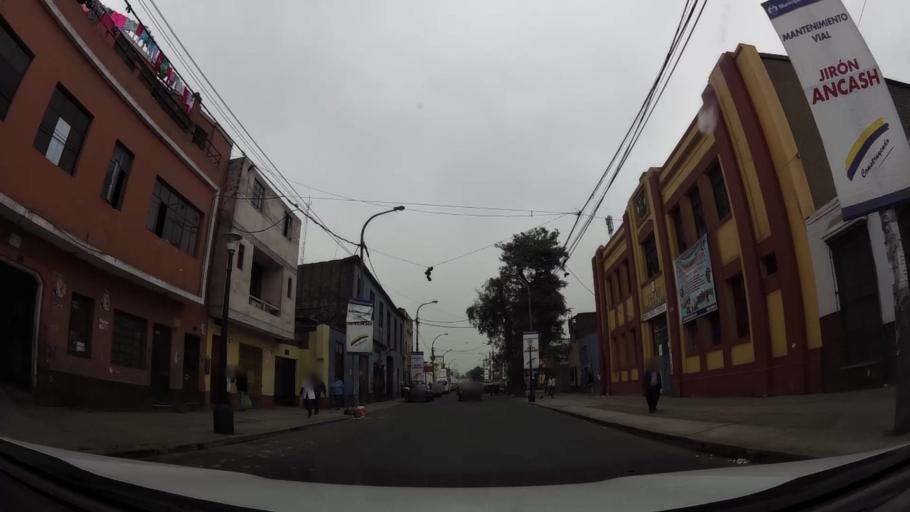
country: PE
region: Lima
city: Lima
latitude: -12.0467
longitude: -77.0168
